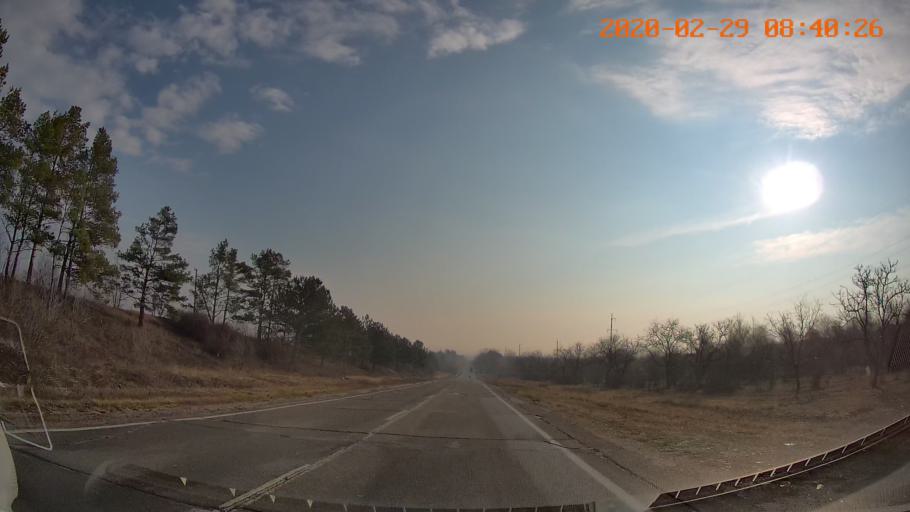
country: MD
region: Anenii Noi
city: Varnita
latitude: 46.9233
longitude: 29.4177
